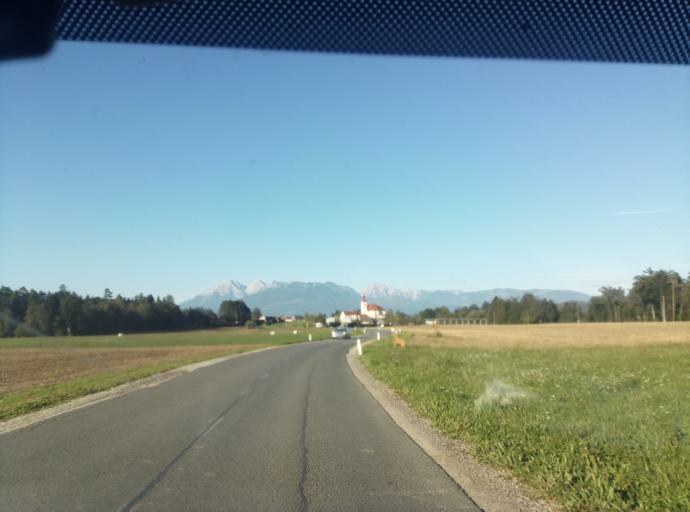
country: SI
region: Medvode
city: Zgornje Pirnice
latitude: 46.1444
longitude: 14.4792
